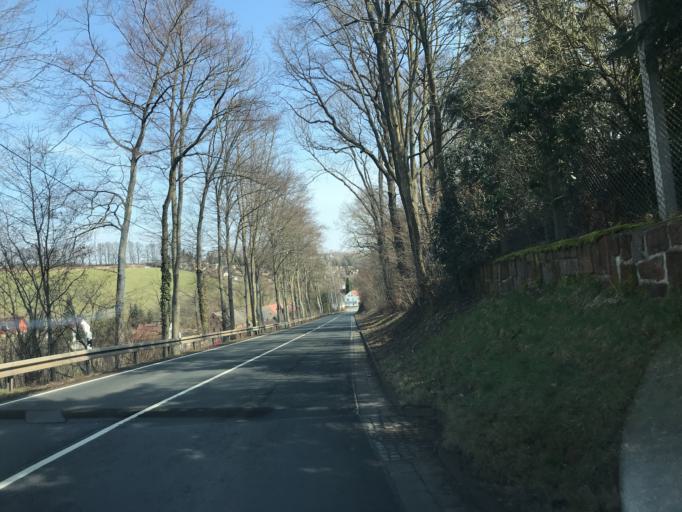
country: DE
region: Saxony
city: Rochlitz
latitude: 51.0427
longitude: 12.7862
